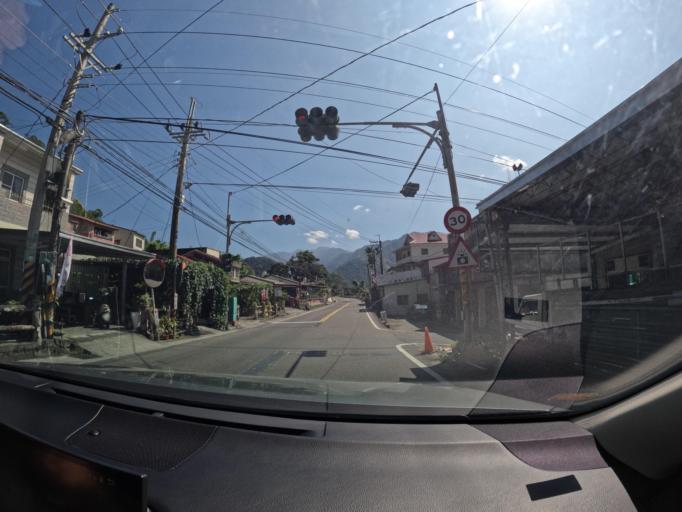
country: TW
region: Taiwan
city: Yujing
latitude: 23.1296
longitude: 120.7174
